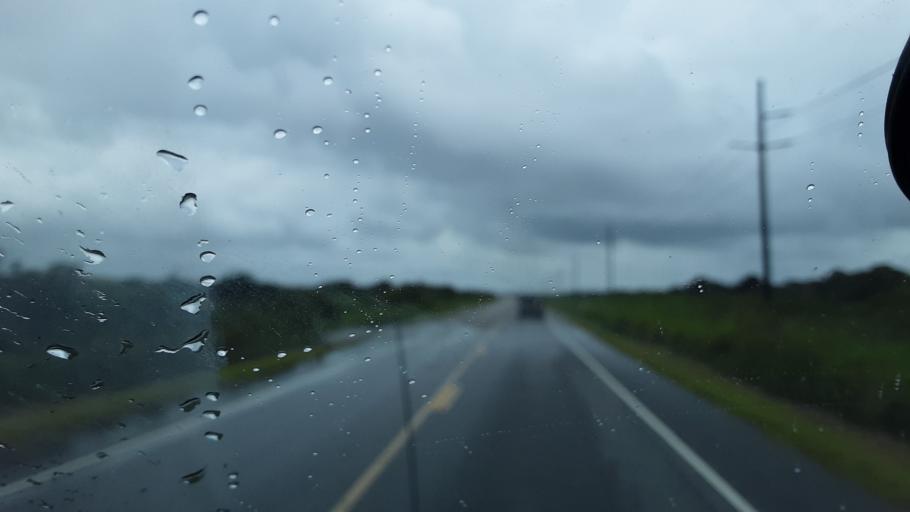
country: US
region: North Carolina
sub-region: Dare County
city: Buxton
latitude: 35.4682
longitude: -75.4836
